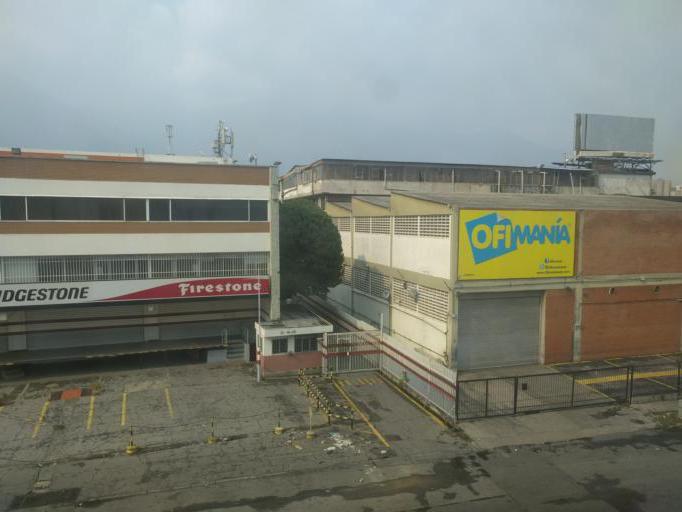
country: VE
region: Miranda
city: El Cafetal
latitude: 10.4808
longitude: -66.8326
